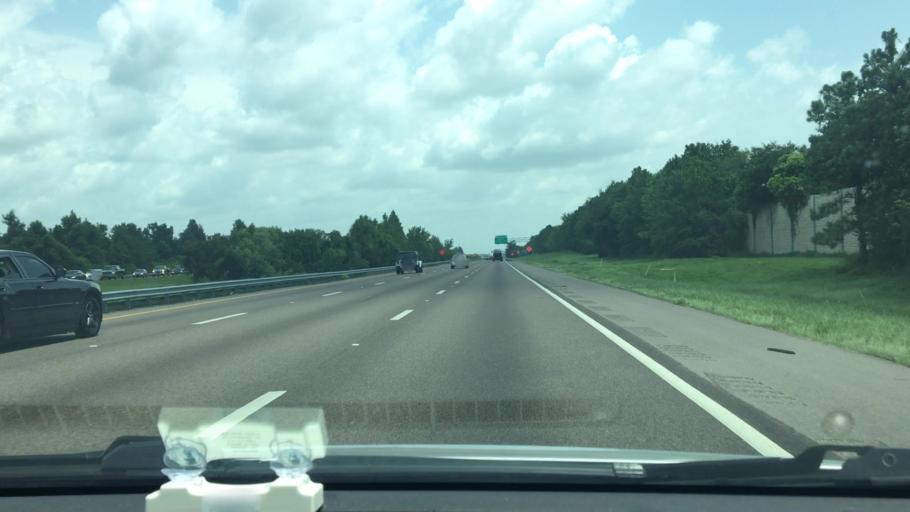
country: US
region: Florida
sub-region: Volusia County
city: Deltona
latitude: 28.8927
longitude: -81.2773
